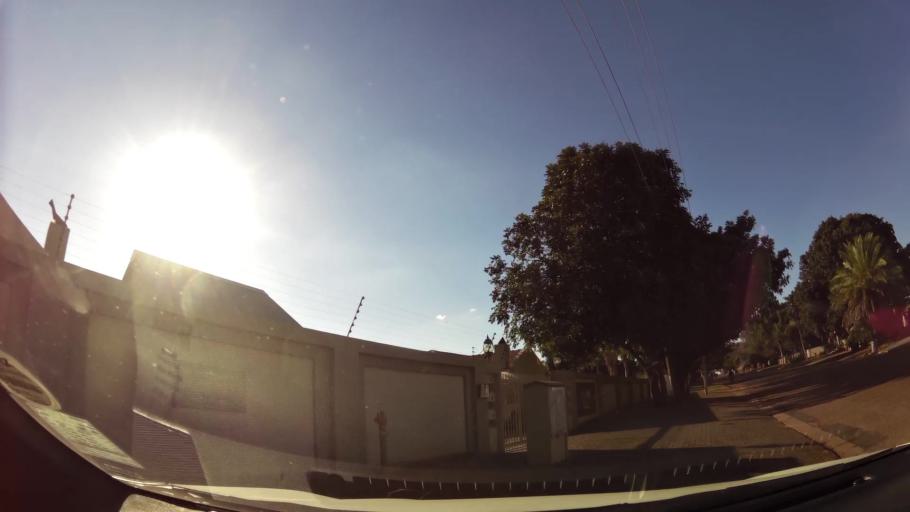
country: ZA
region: Limpopo
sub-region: Waterberg District Municipality
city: Mokopane
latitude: -24.1828
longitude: 29.0041
